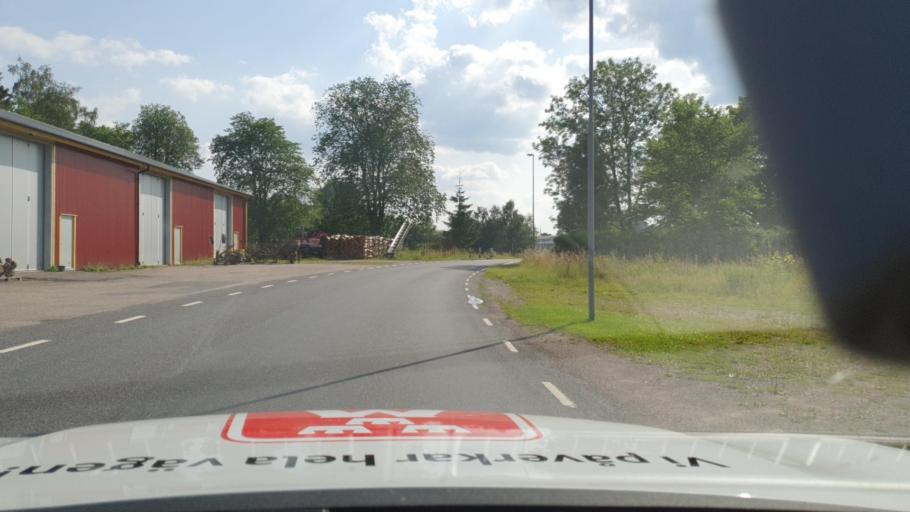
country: SE
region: Vaestra Goetaland
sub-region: Falkopings Kommun
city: Falkoeping
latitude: 58.0208
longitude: 13.5750
